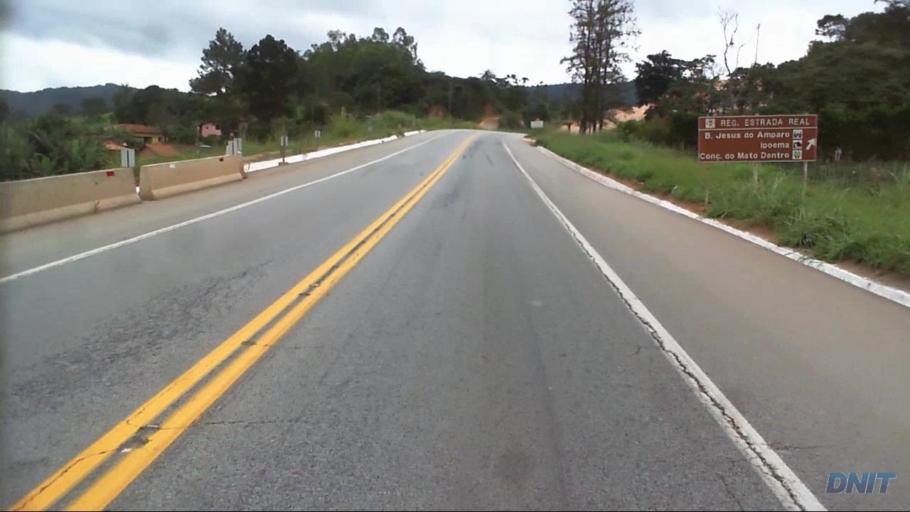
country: BR
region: Minas Gerais
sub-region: Barao De Cocais
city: Barao de Cocais
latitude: -19.7429
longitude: -43.5018
